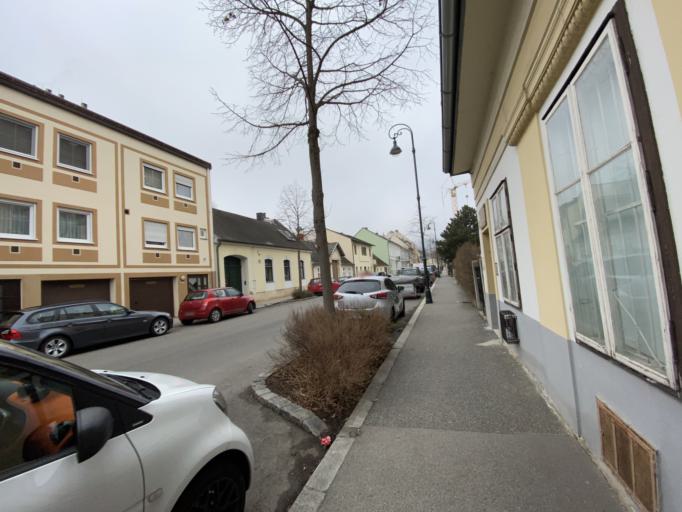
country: AT
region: Lower Austria
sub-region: Politischer Bezirk Baden
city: Baden
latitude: 48.0040
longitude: 16.2342
